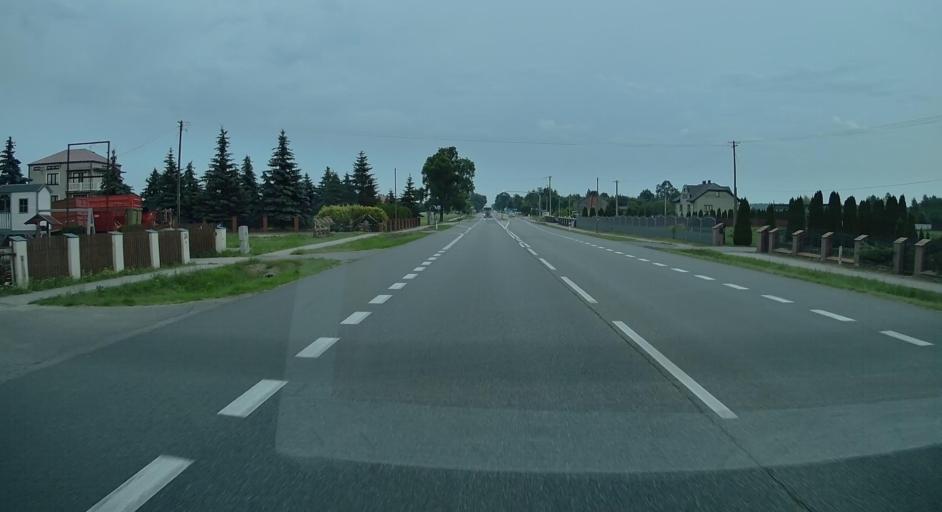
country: PL
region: Masovian Voivodeship
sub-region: Powiat siedlecki
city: Zbuczyn
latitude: 52.1094
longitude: 22.3837
